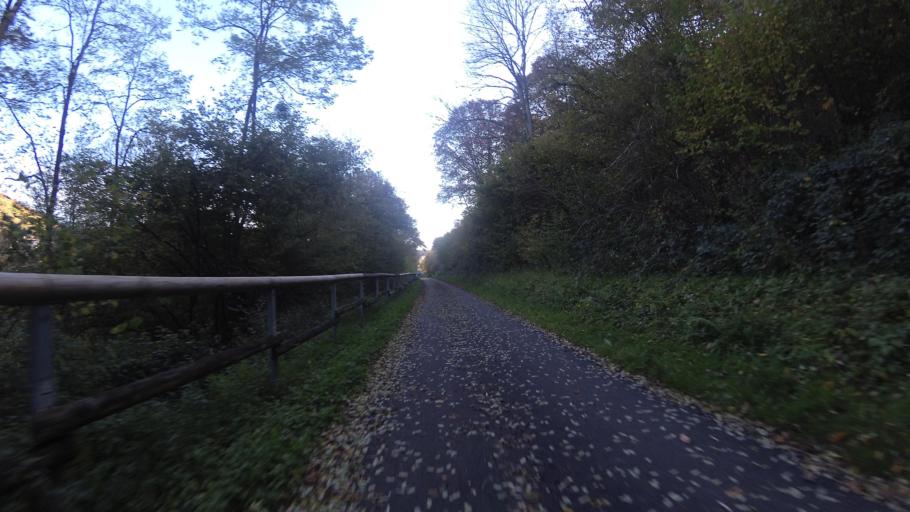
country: DE
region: Rheinland-Pfalz
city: Waldrach
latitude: 49.7518
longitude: 6.7376
